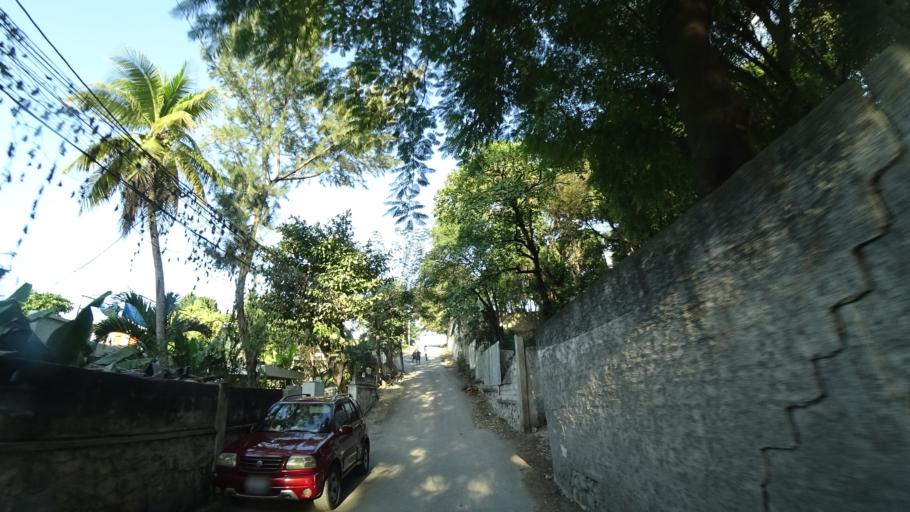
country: HT
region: Ouest
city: Port-au-Prince
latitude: 18.5308
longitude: -72.3212
